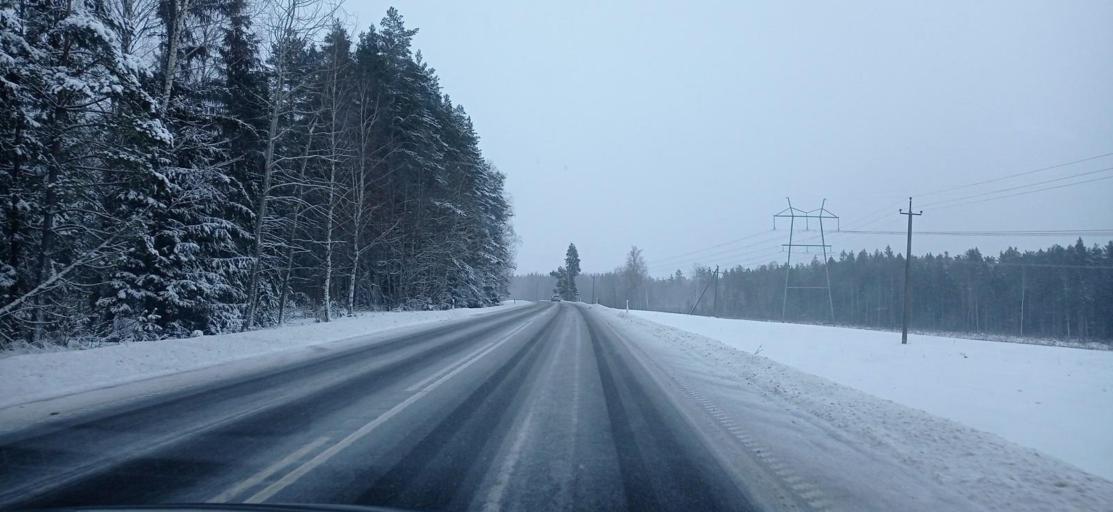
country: EE
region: Viljandimaa
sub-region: Abja vald
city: Abja-Paluoja
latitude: 58.2660
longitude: 25.2542
